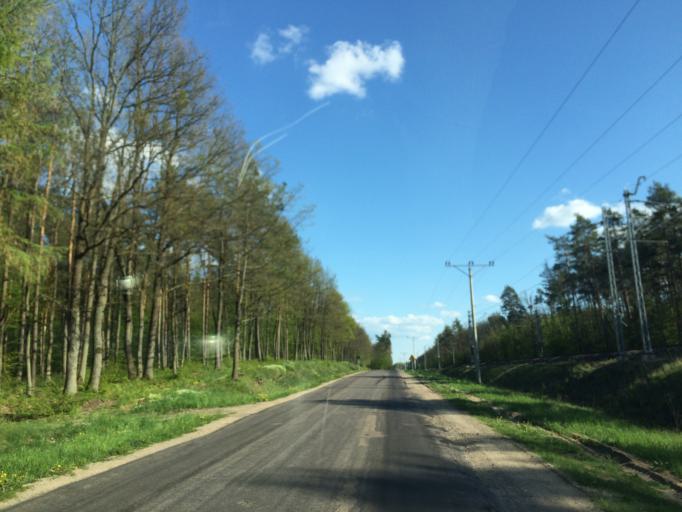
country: PL
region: Warmian-Masurian Voivodeship
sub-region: Powiat dzialdowski
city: Rybno
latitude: 53.3661
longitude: 19.9389
